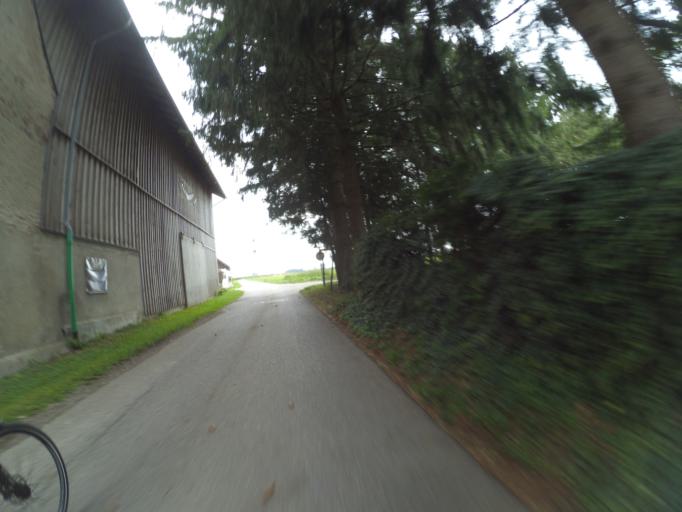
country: DE
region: Bavaria
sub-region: Swabia
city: Buchloe
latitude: 48.0466
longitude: 10.7736
